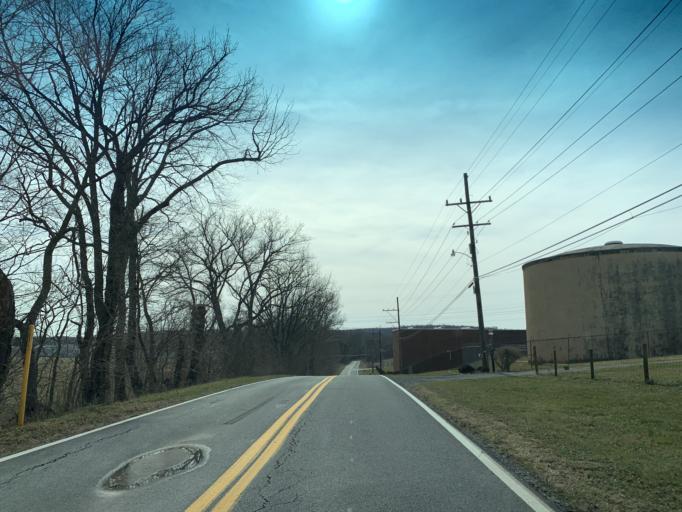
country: US
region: Maryland
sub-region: Frederick County
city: Adamstown
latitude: 39.2568
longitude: -77.4783
